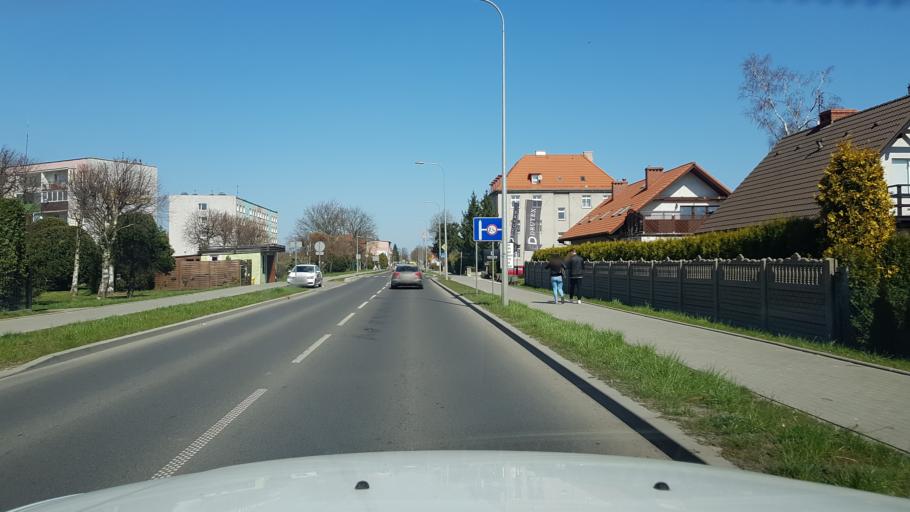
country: PL
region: West Pomeranian Voivodeship
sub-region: Powiat slawienski
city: Slawno
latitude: 54.3586
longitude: 16.6740
